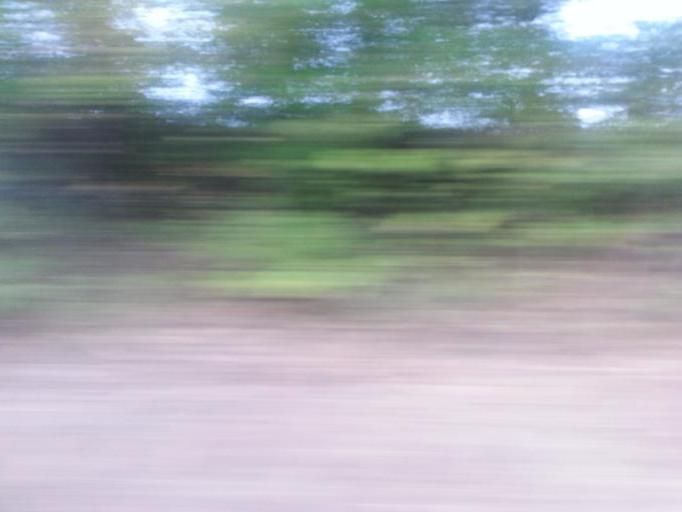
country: US
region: Tennessee
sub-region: Campbell County
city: Caryville
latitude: 36.2680
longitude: -84.1890
